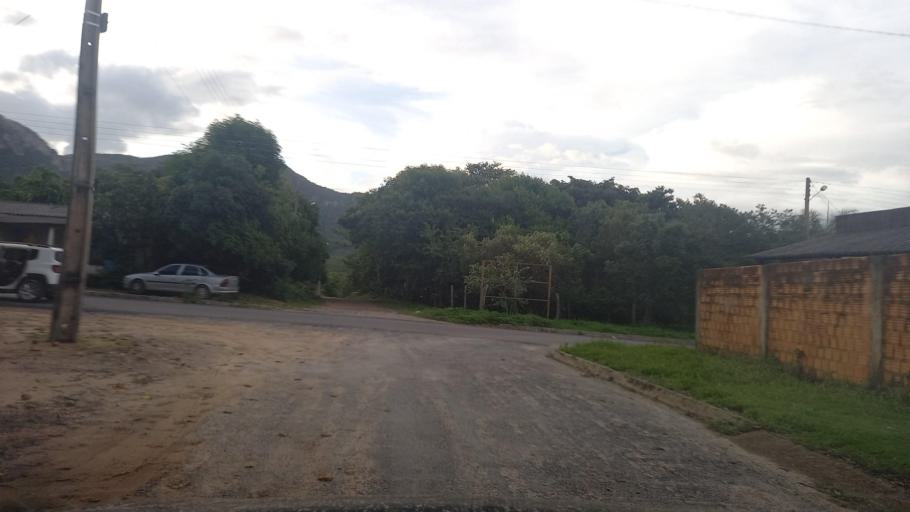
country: BR
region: Goias
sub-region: Cavalcante
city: Cavalcante
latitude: -13.7895
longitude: -47.4603
